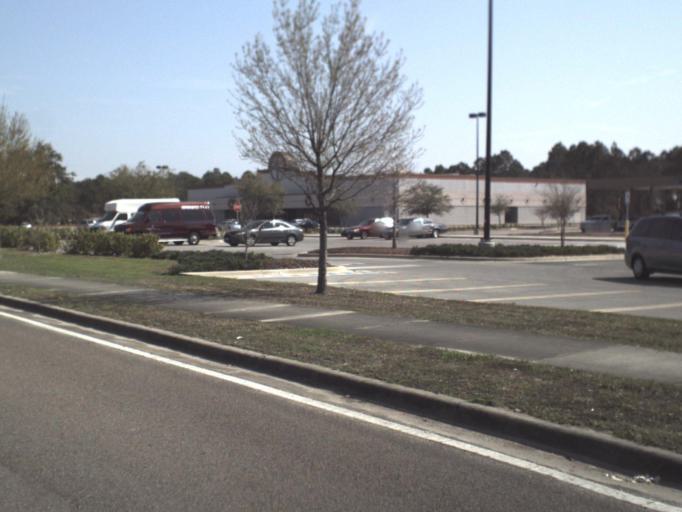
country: US
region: Florida
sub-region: Bay County
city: Pretty Bayou
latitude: 30.1898
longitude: -85.6879
